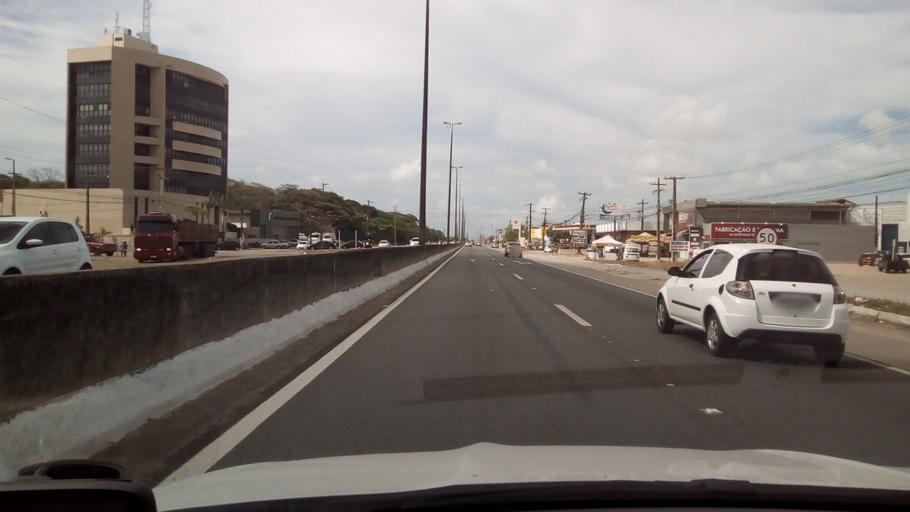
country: BR
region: Paraiba
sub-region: Joao Pessoa
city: Joao Pessoa
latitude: -7.0708
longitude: -34.8497
